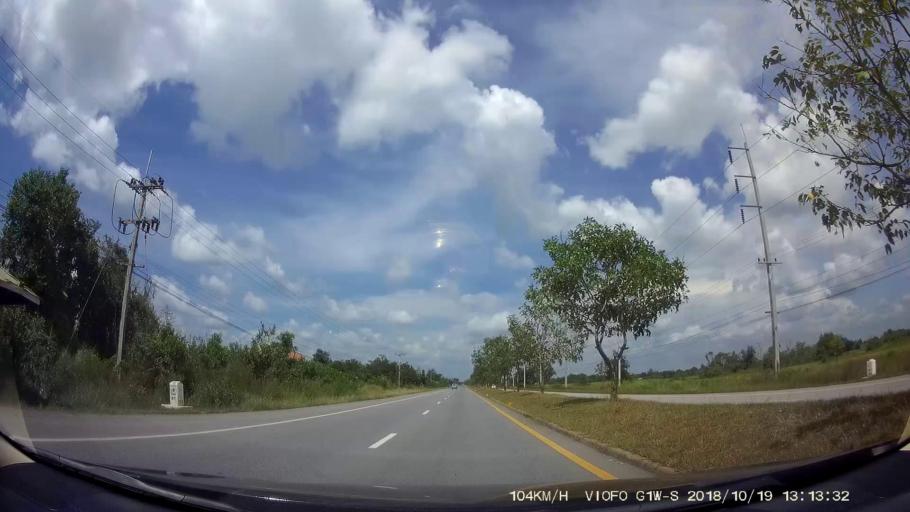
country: TH
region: Nakhon Ratchasima
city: Dan Khun Thot
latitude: 15.3613
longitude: 101.8300
